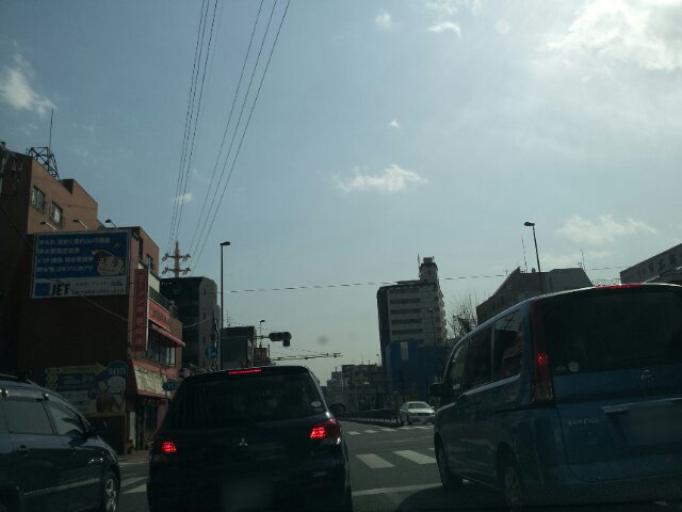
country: JP
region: Kanagawa
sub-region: Kawasaki-shi
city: Kawasaki
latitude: 35.5637
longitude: 139.6966
